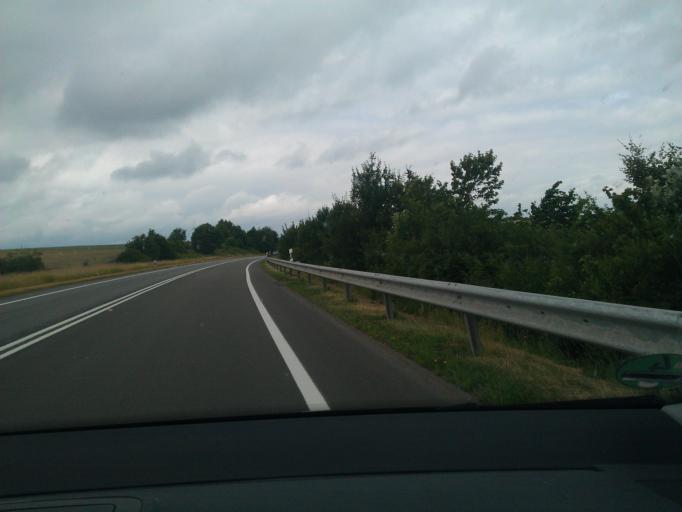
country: DE
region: Rheinland-Pfalz
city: Obernheim-Kirchenarnbach
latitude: 49.3572
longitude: 7.6044
